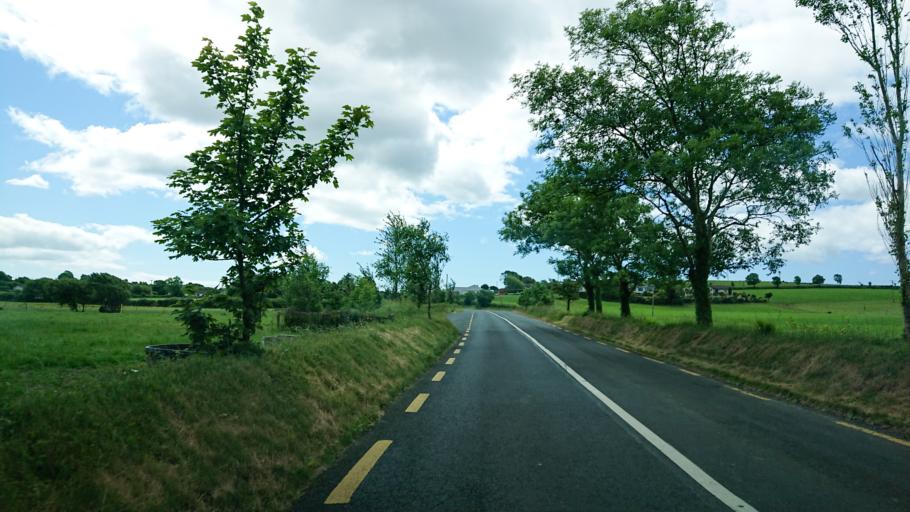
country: IE
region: Munster
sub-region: Waterford
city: Tra Mhor
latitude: 52.2164
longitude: -7.1967
